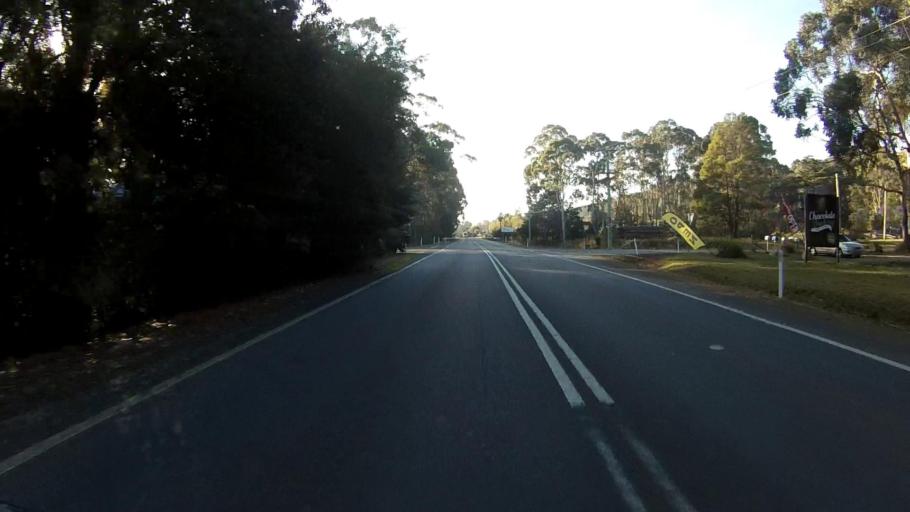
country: AU
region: Tasmania
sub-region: Clarence
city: Sandford
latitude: -43.0585
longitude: 147.8650
